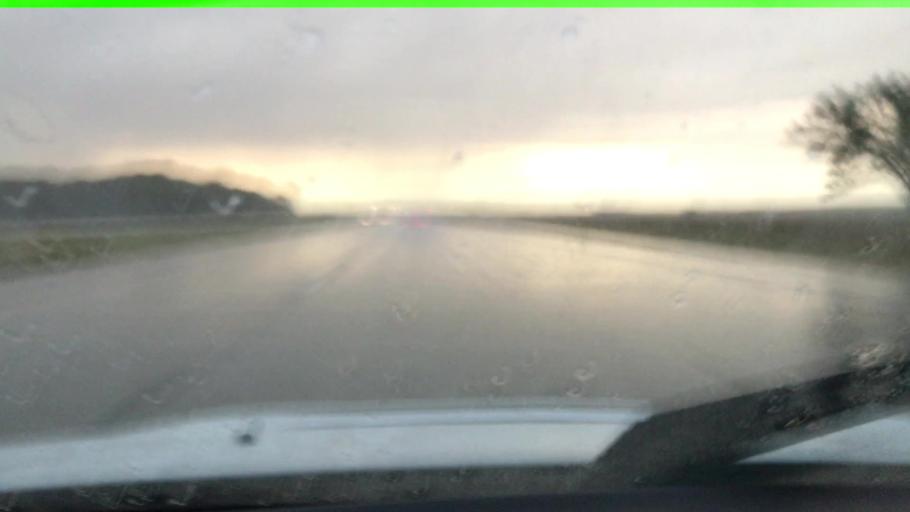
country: US
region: Nebraska
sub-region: Lancaster County
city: Waverly
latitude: 40.8967
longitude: -96.5964
